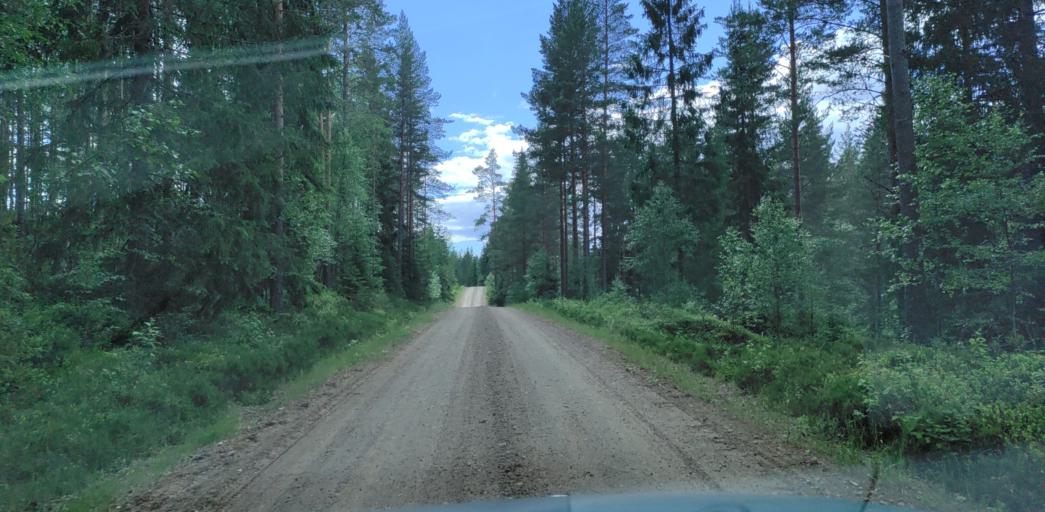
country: SE
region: Vaermland
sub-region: Hagfors Kommun
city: Ekshaerad
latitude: 60.0798
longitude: 13.2929
